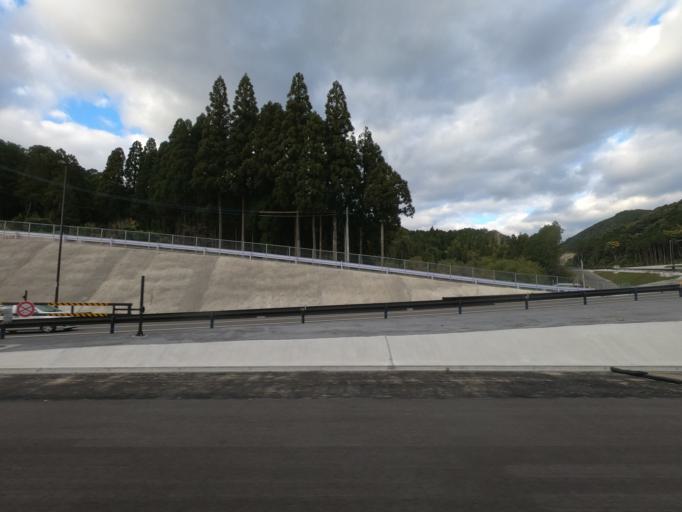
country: JP
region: Kumamoto
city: Minamata
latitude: 32.2110
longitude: 130.4238
